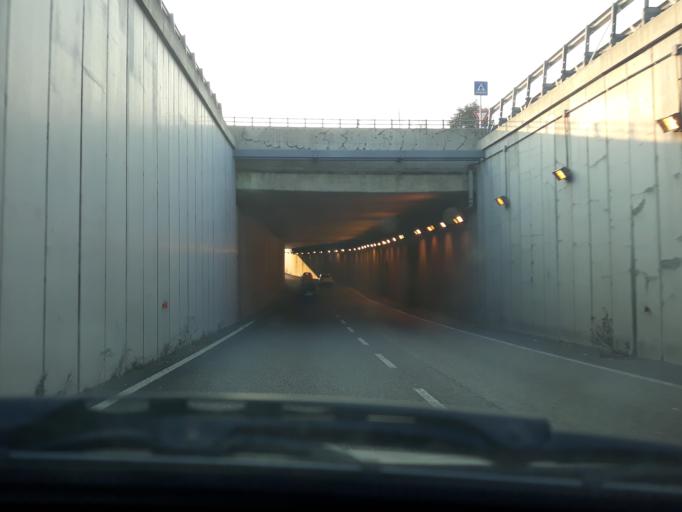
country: IT
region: Lombardy
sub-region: Provincia di Monza e Brianza
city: Monza
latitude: 45.5672
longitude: 9.2859
